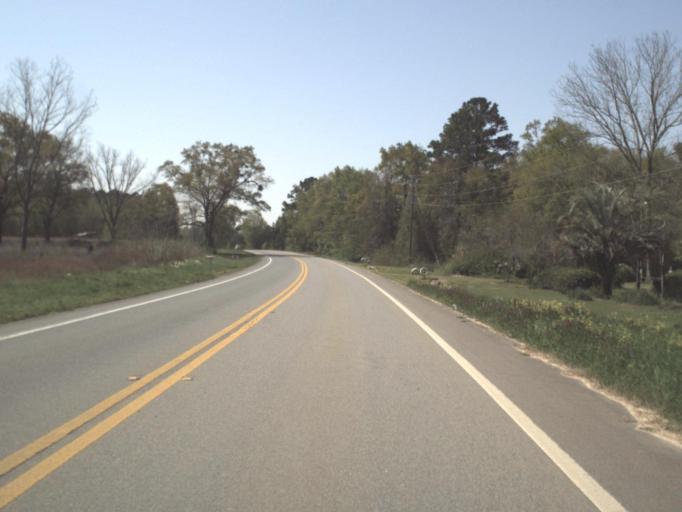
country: US
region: Florida
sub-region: Jackson County
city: Graceville
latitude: 30.9237
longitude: -85.4274
